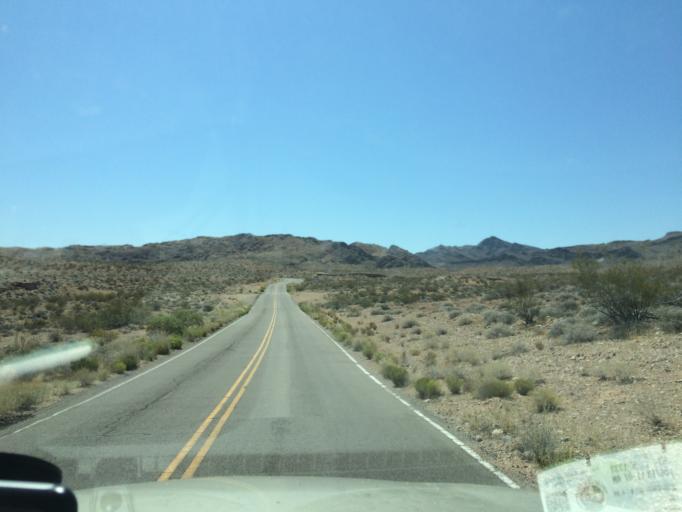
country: US
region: Nevada
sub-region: Clark County
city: Moapa Valley
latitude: 36.4347
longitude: -114.6377
